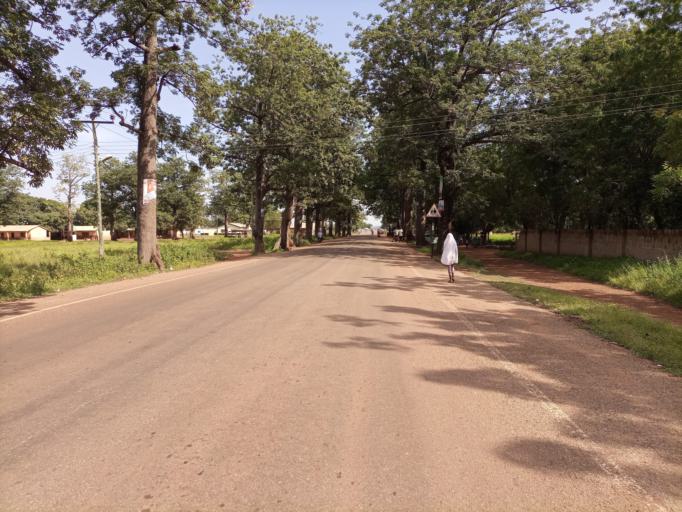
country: GH
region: Northern
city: Savelugu
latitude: 9.5564
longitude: -0.9465
